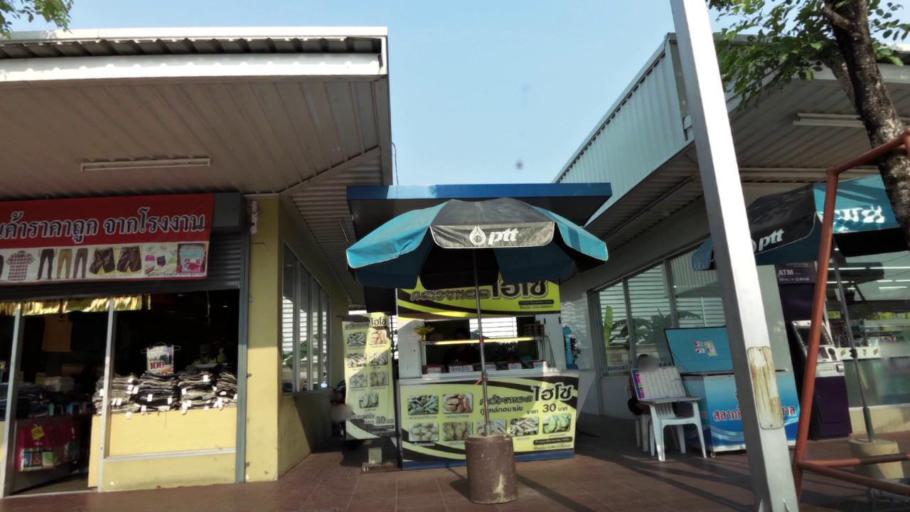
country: TH
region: Phra Nakhon Si Ayutthaya
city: Uthai
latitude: 14.3268
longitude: 100.6285
